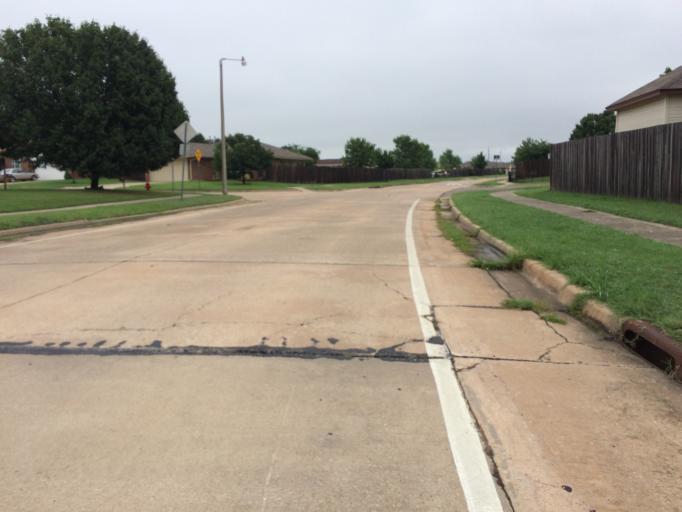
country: US
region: Oklahoma
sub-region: Cleveland County
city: Hall Park
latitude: 35.2077
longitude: -97.4125
